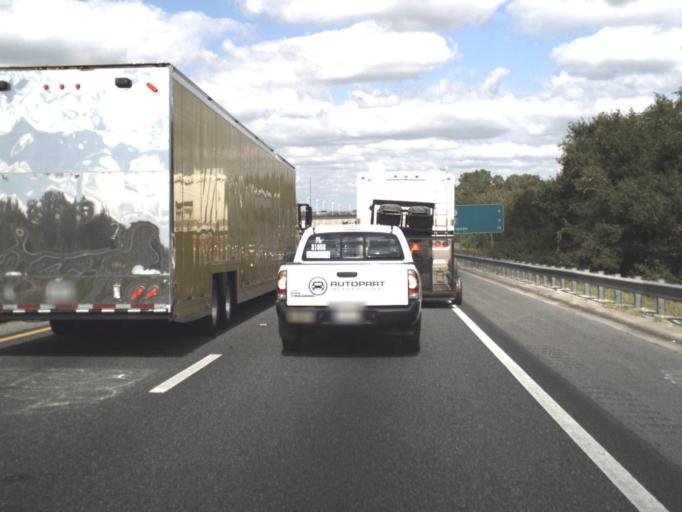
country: US
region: Florida
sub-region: Orange County
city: Meadow Woods
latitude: 28.3561
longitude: -81.3863
